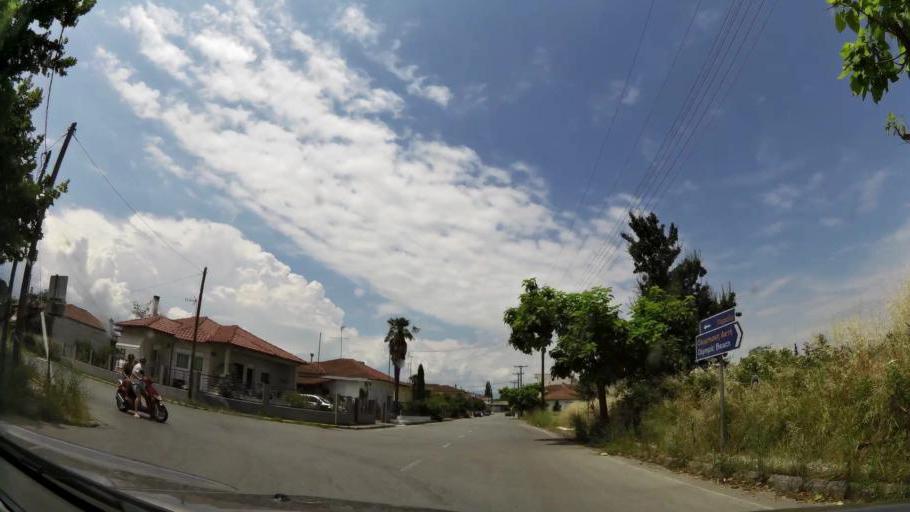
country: GR
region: Central Macedonia
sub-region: Nomos Pierias
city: Peristasi
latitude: 40.2652
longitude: 22.5351
